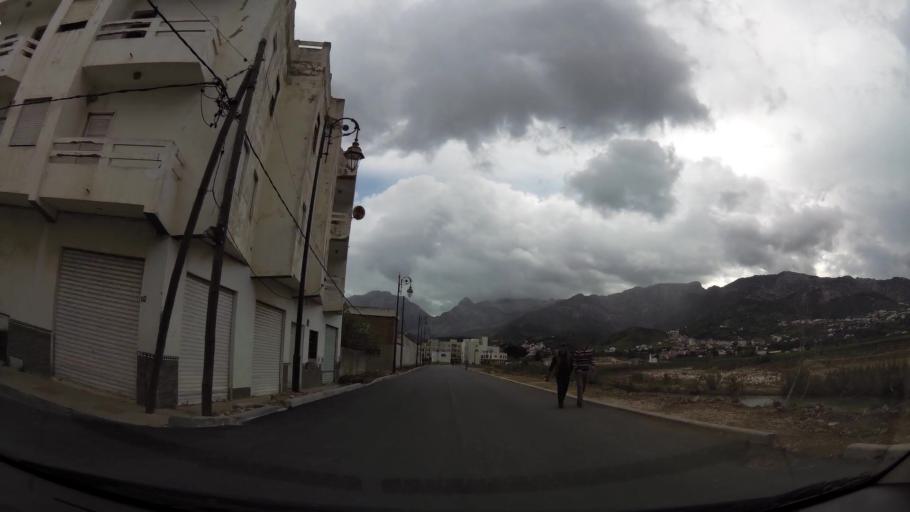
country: MA
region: Tanger-Tetouan
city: Tetouan
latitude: 35.5622
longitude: -5.3496
